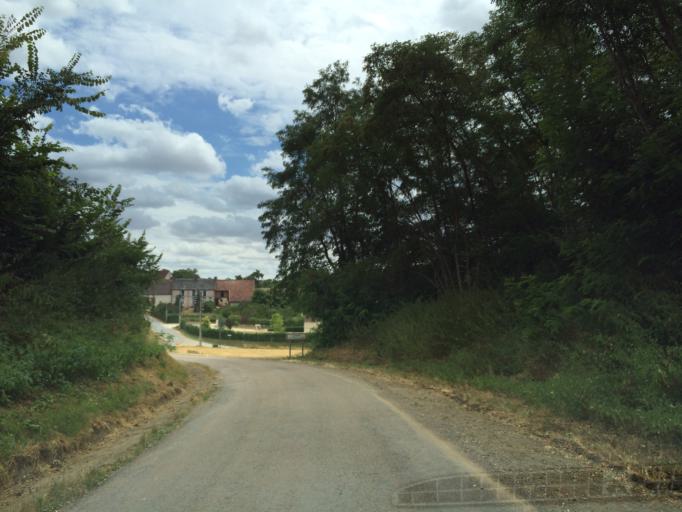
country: FR
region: Bourgogne
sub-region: Departement de l'Yonne
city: Fleury-la-Vallee
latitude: 47.8490
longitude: 3.4042
